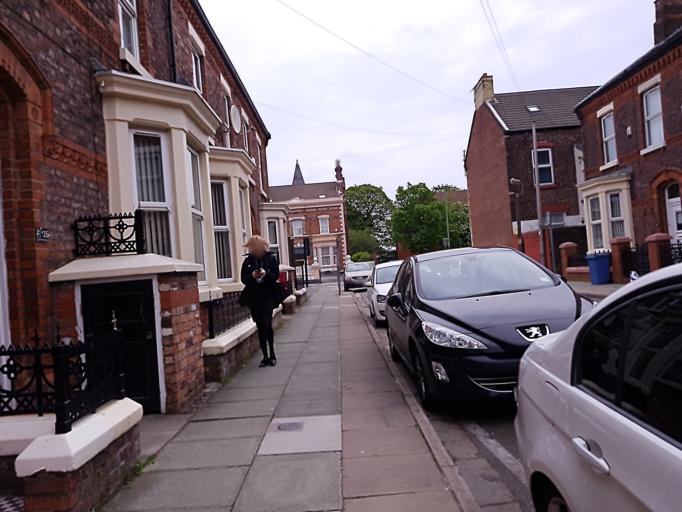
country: GB
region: England
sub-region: Liverpool
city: Liverpool
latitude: 53.4305
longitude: -2.9593
